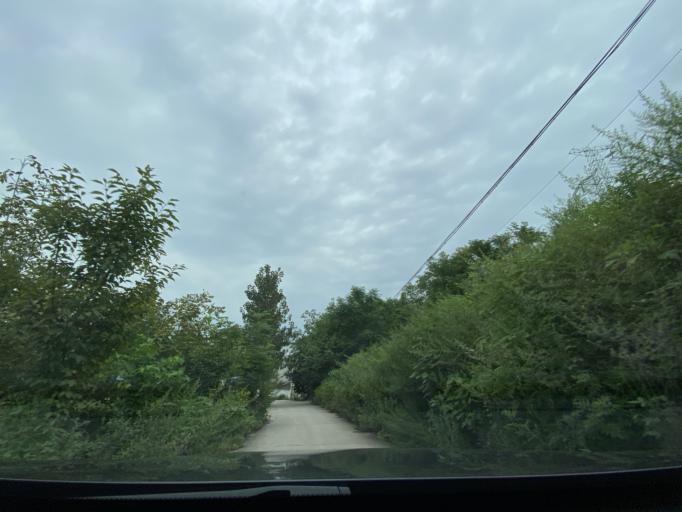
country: CN
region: Sichuan
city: Jiancheng
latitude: 30.3879
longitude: 104.4965
